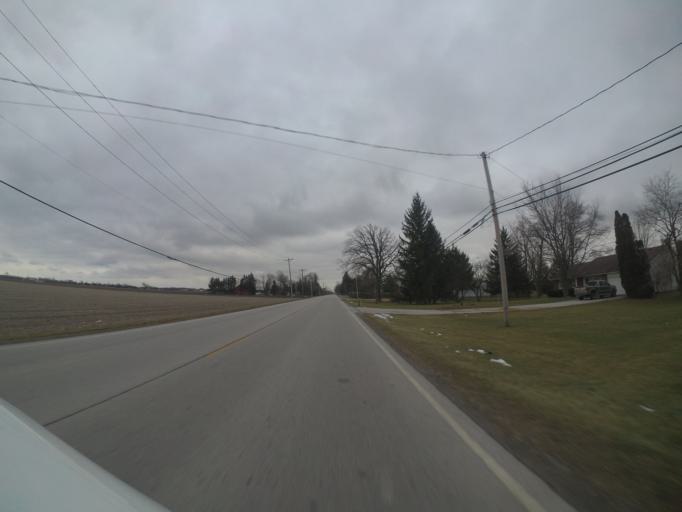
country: US
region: Ohio
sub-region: Wood County
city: Walbridge
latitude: 41.5856
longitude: -83.5125
